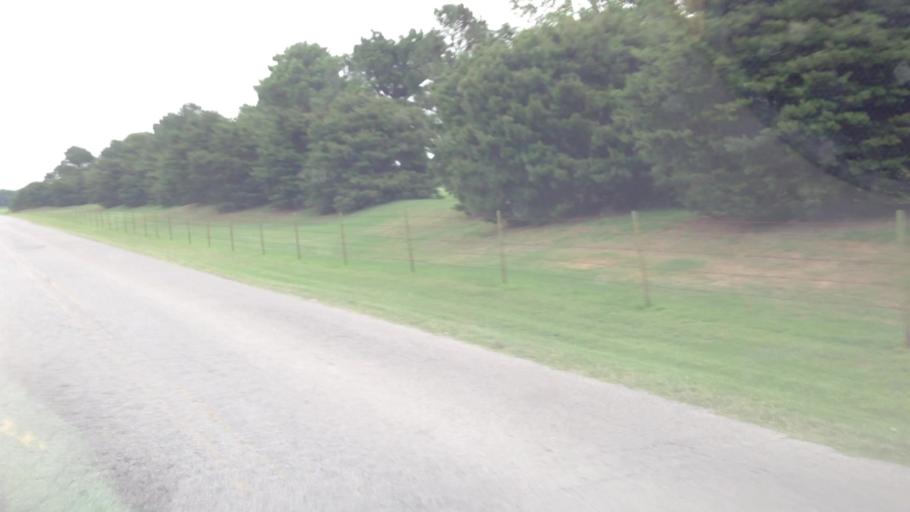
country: US
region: Oklahoma
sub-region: Delaware County
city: Cleora
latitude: 36.5465
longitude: -94.9618
